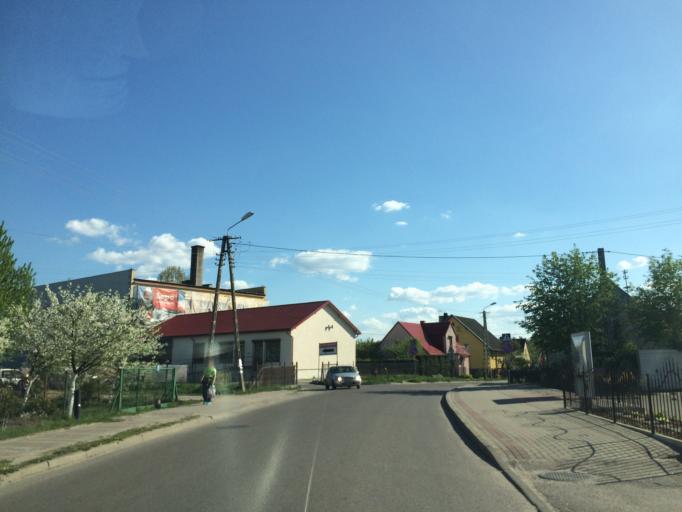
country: PL
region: Warmian-Masurian Voivodeship
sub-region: Powiat dzialdowski
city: Rybno
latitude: 53.3860
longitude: 19.9305
